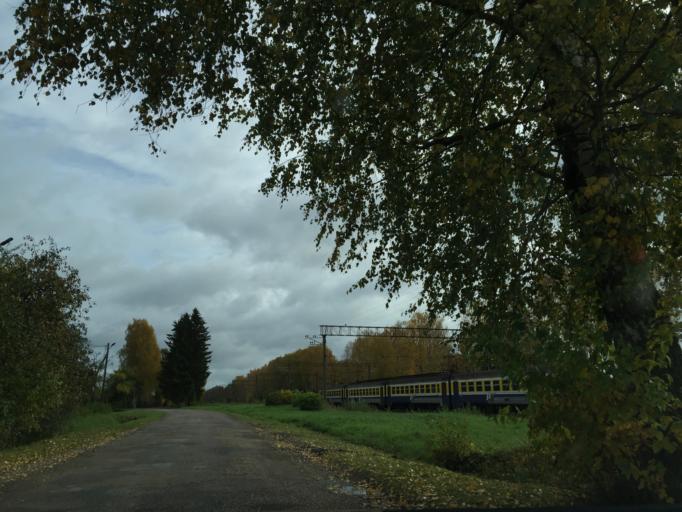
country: LV
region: Lielvarde
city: Lielvarde
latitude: 56.7222
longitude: 24.8106
